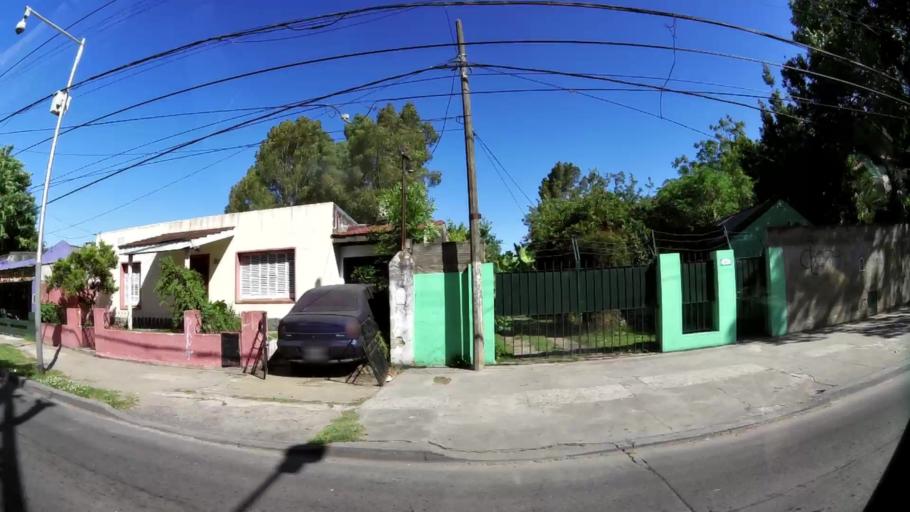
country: AR
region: Buenos Aires
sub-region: Partido de San Isidro
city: San Isidro
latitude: -34.4702
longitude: -58.5326
